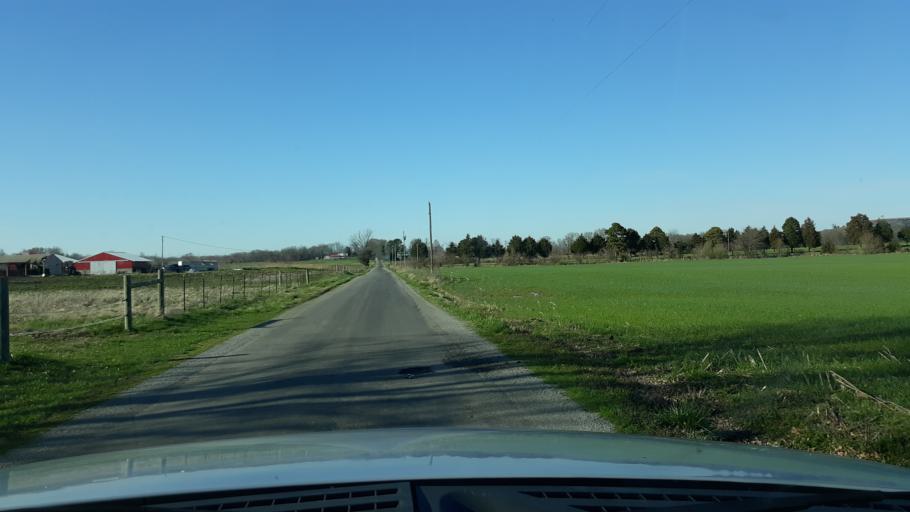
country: US
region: Illinois
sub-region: Saline County
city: Harrisburg
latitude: 37.7980
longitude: -88.6055
